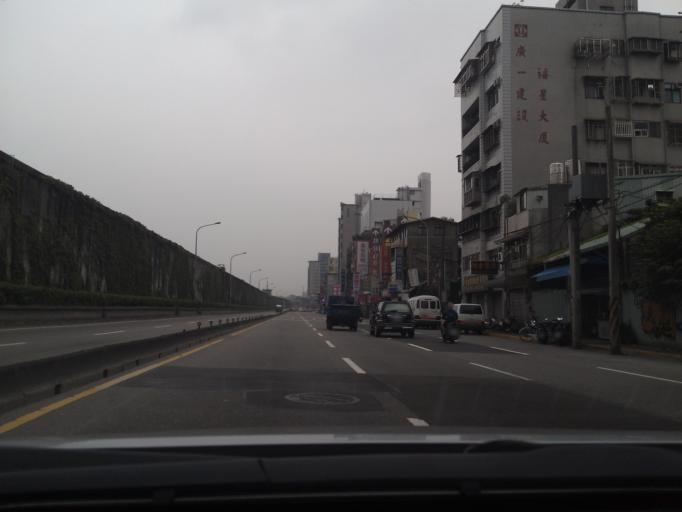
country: TW
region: Taipei
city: Taipei
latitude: 25.0646
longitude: 121.5088
